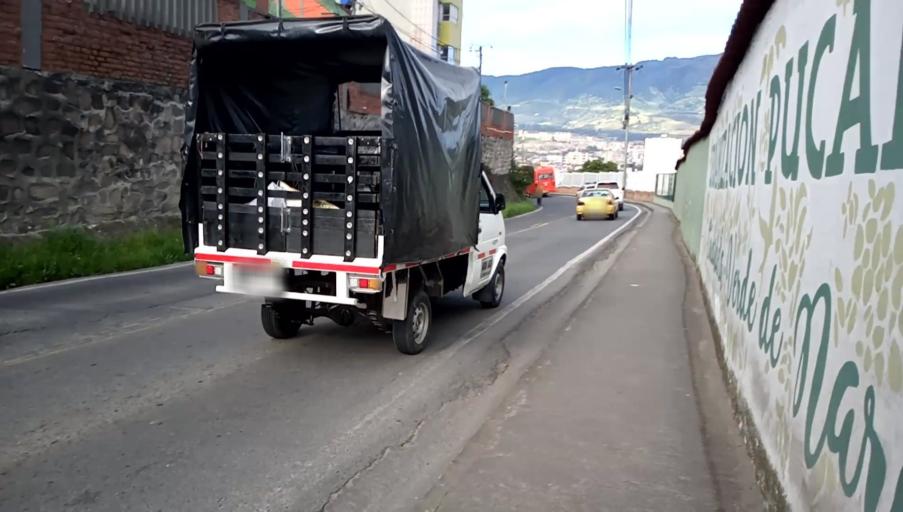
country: CO
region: Narino
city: Puerres
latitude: 1.2057
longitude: -77.2566
